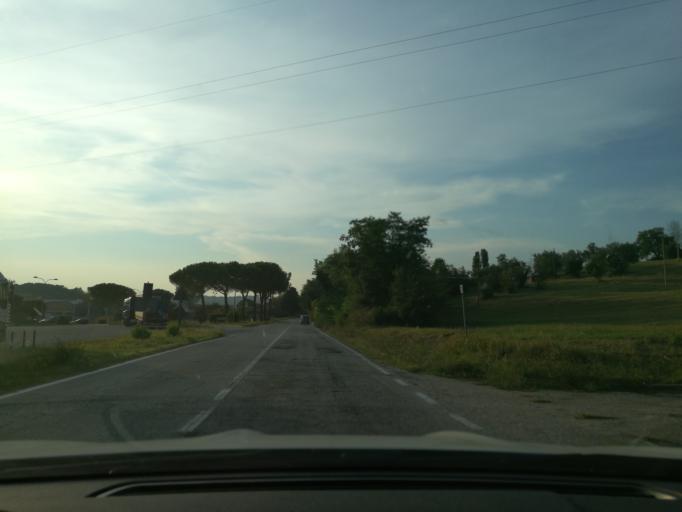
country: IT
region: Umbria
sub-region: Provincia di Terni
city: San Gemini
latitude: 42.6325
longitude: 12.5525
